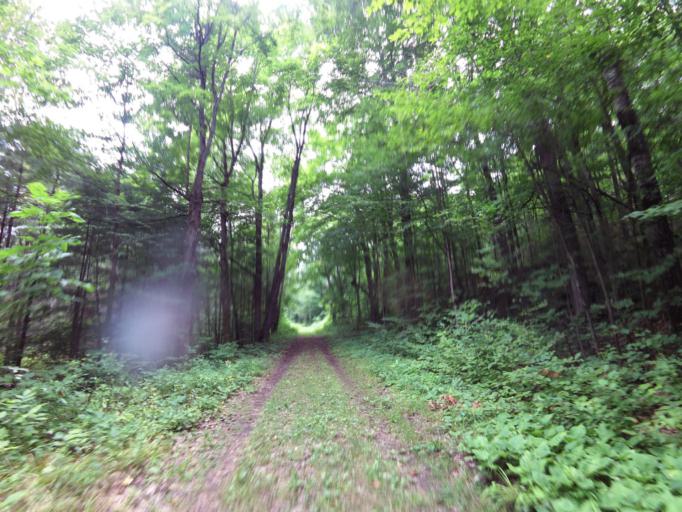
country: CA
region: Quebec
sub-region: Outaouais
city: Wakefield
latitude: 45.6171
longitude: -76.0397
